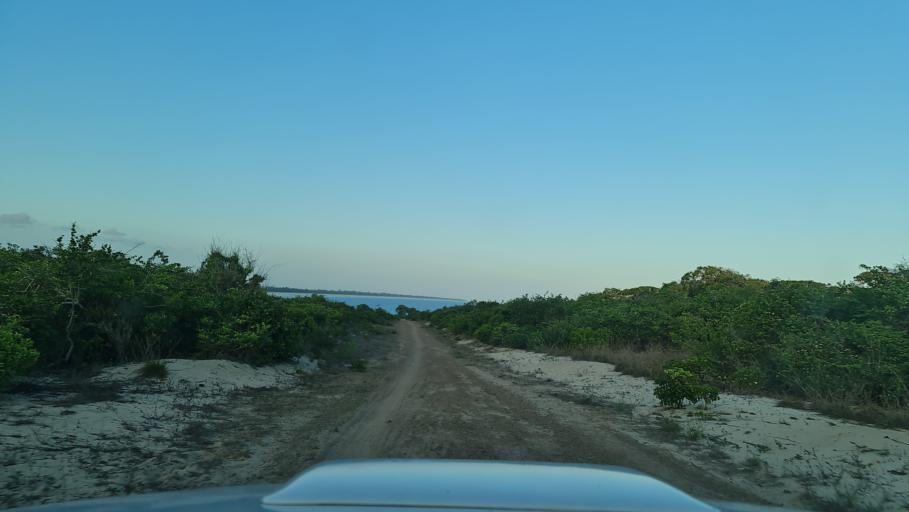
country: MZ
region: Nampula
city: Ilha de Mocambique
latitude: -15.6304
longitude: 40.4203
